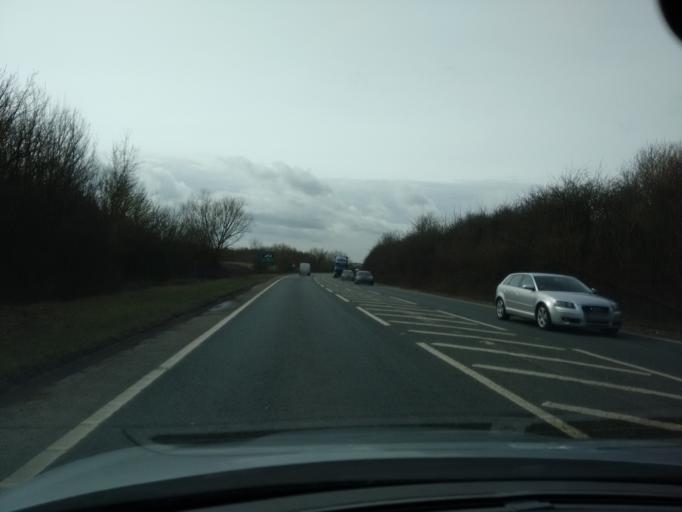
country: GB
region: England
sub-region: Worcestershire
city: Evesham
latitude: 52.0794
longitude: -1.9312
